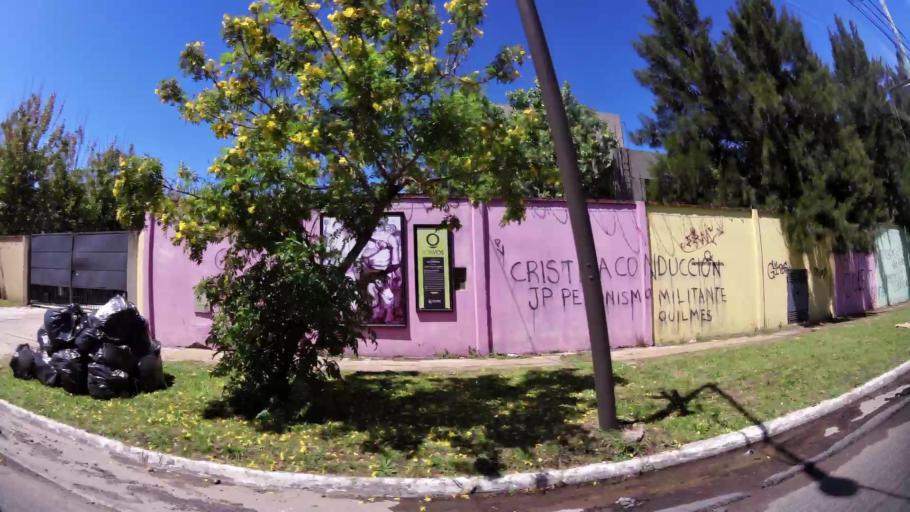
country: AR
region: Buenos Aires
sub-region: Partido de Quilmes
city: Quilmes
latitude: -34.7291
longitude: -58.2813
